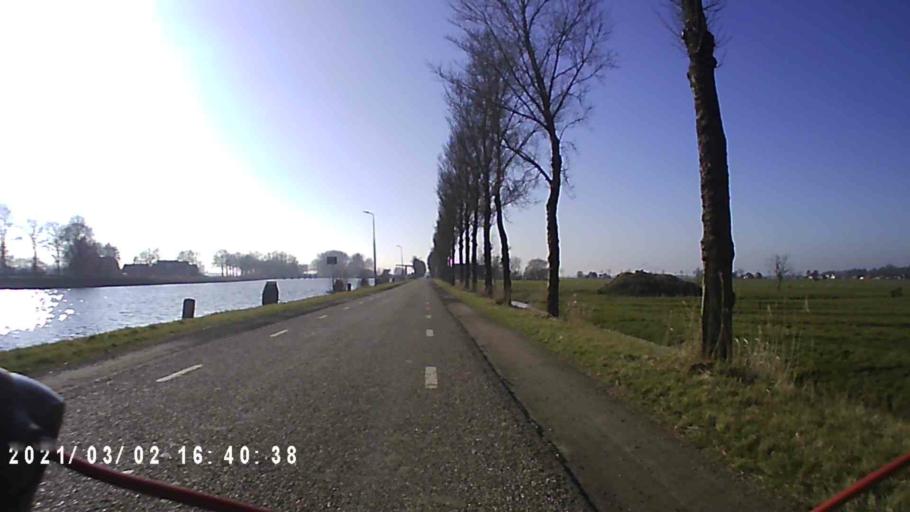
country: NL
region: Groningen
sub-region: Gemeente Zuidhorn
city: Grijpskerk
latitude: 53.2503
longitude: 6.3225
